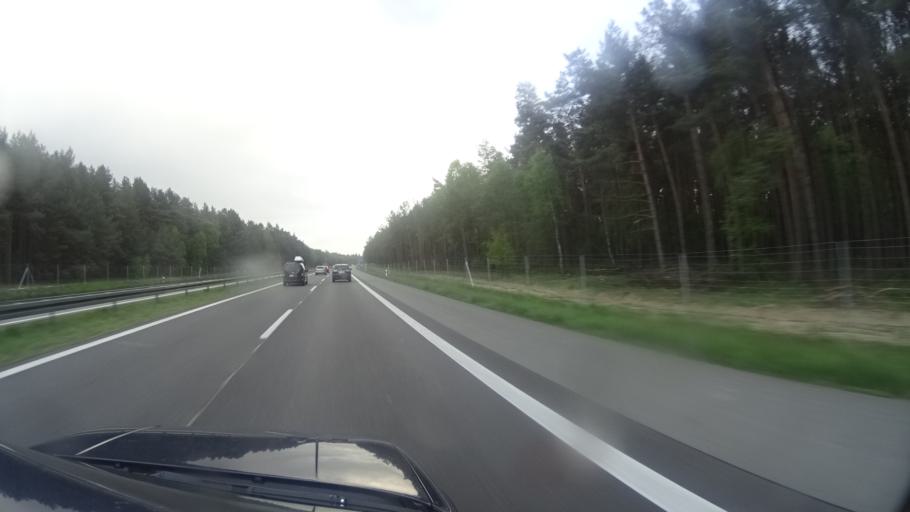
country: DE
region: Brandenburg
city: Wittstock
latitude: 53.0806
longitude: 12.5226
